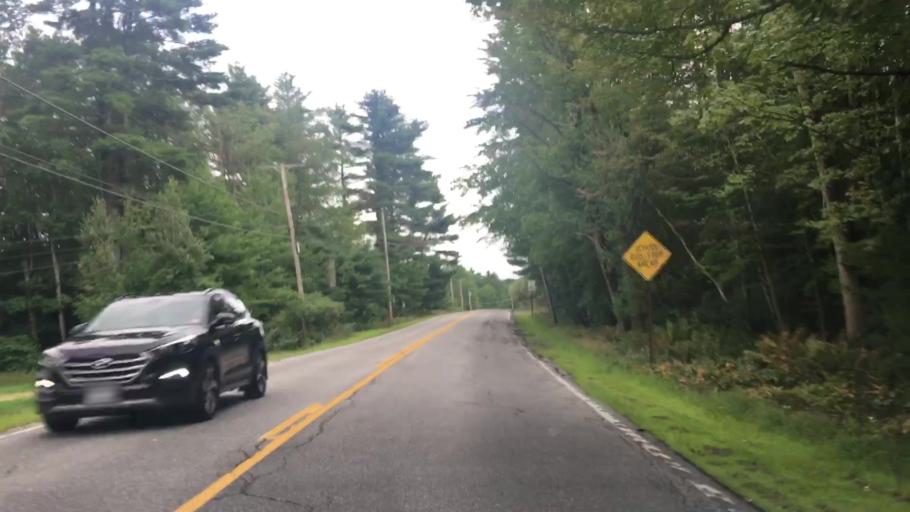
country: US
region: Maine
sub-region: York County
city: Lake Arrowhead
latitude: 43.6557
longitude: -70.7622
